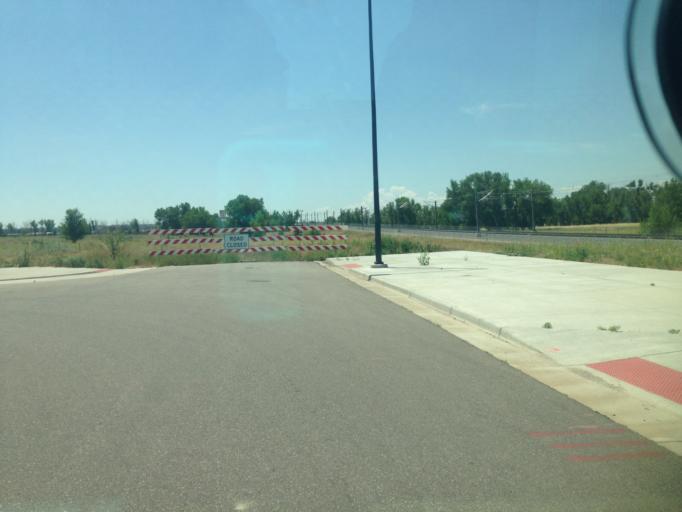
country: US
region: Colorado
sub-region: Adams County
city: Aurora
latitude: 39.8057
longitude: -104.7834
